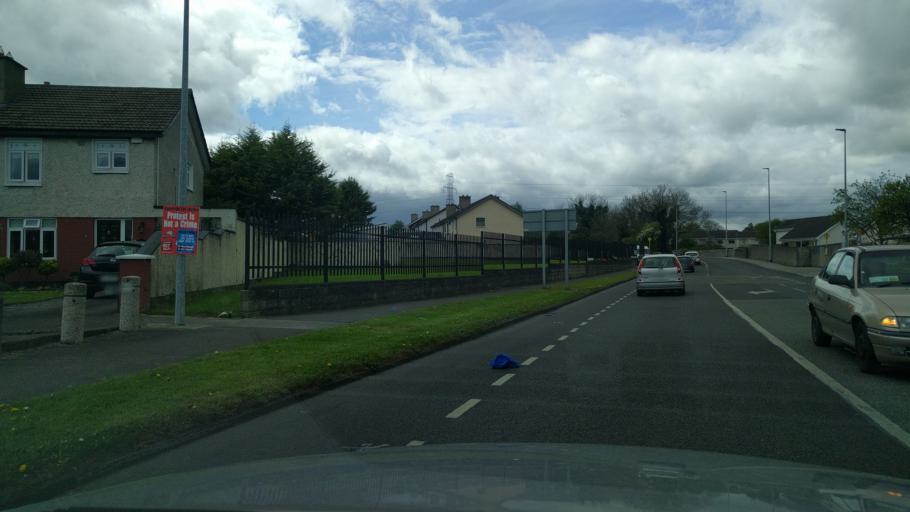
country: IE
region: Leinster
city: Firhouse
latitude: 53.3012
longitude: -6.3523
